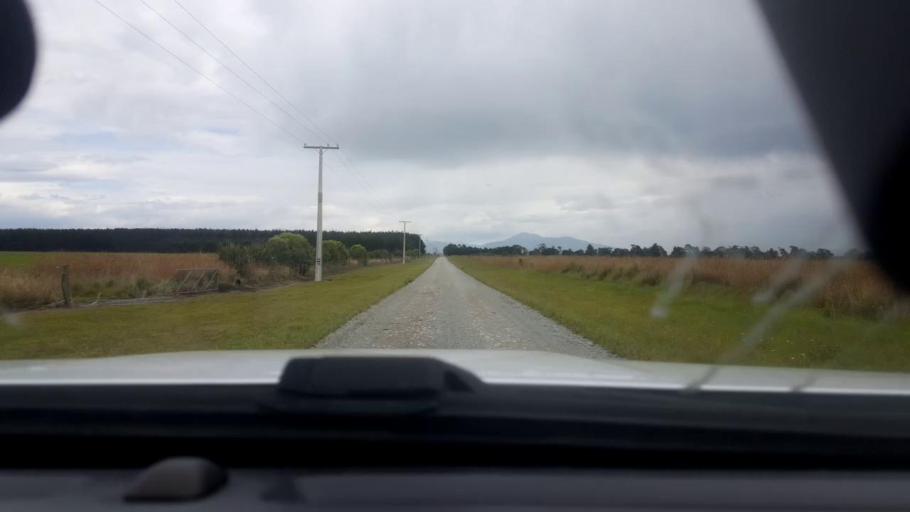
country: NZ
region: Canterbury
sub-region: Timaru District
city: Timaru
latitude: -44.1647
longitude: 171.4085
